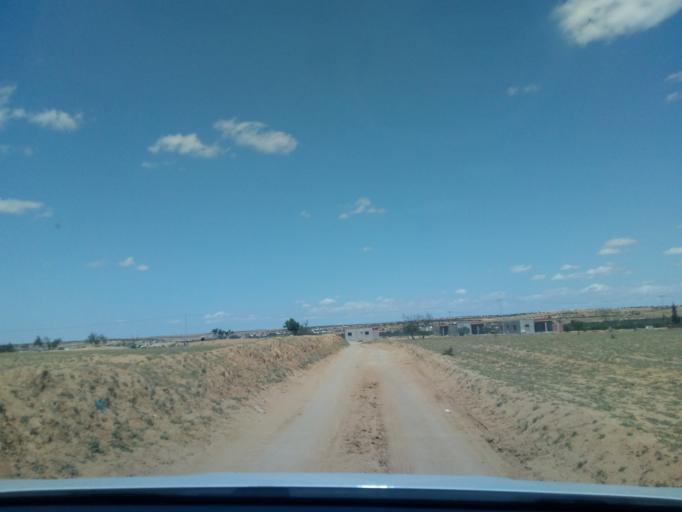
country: TN
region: Safaqis
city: Sfax
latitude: 34.7313
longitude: 10.4971
